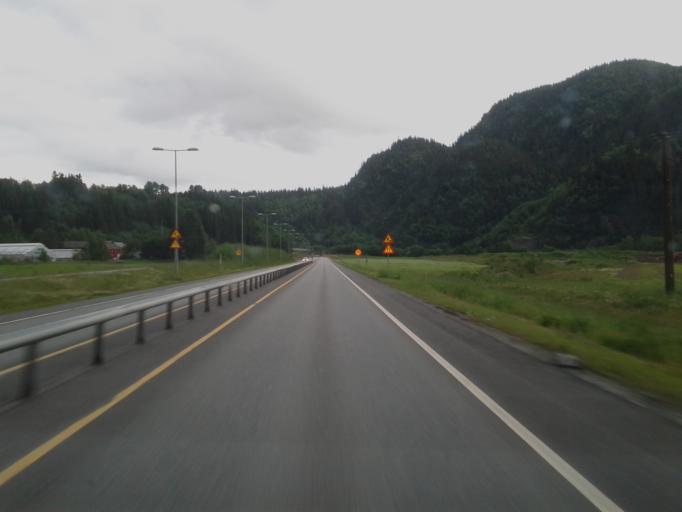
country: NO
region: Sor-Trondelag
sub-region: Midtre Gauldal
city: Storen
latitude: 63.0752
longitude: 10.2627
